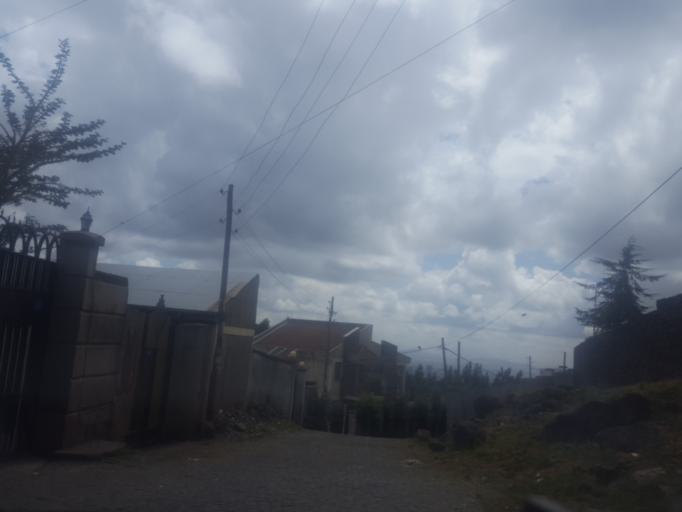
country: ET
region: Adis Abeba
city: Addis Ababa
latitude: 9.0651
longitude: 38.7351
